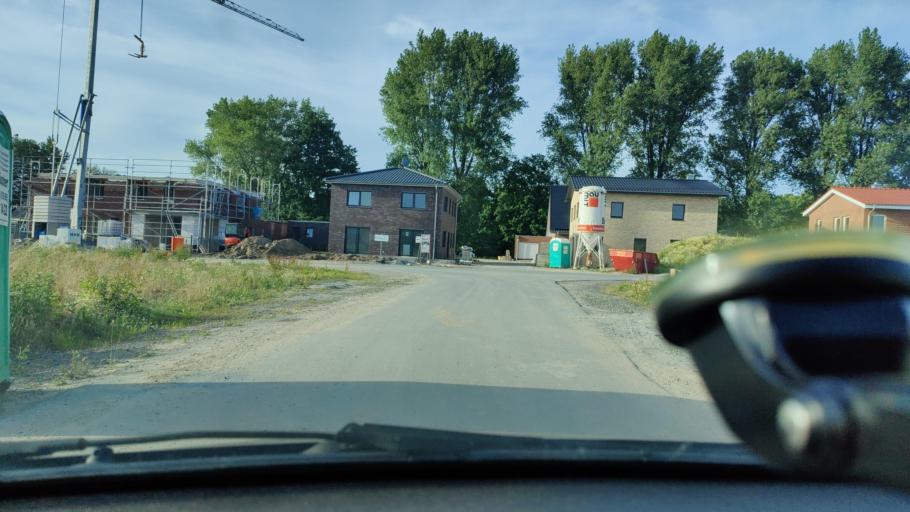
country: DE
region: North Rhine-Westphalia
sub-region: Regierungsbezirk Munster
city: Billerbeck
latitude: 51.9776
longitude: 7.2792
